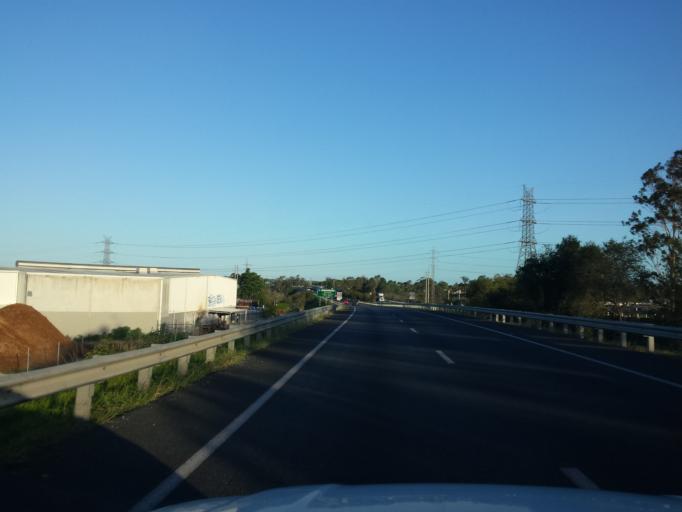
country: AU
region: Queensland
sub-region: Logan
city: Logan City
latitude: -27.6678
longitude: 153.1142
